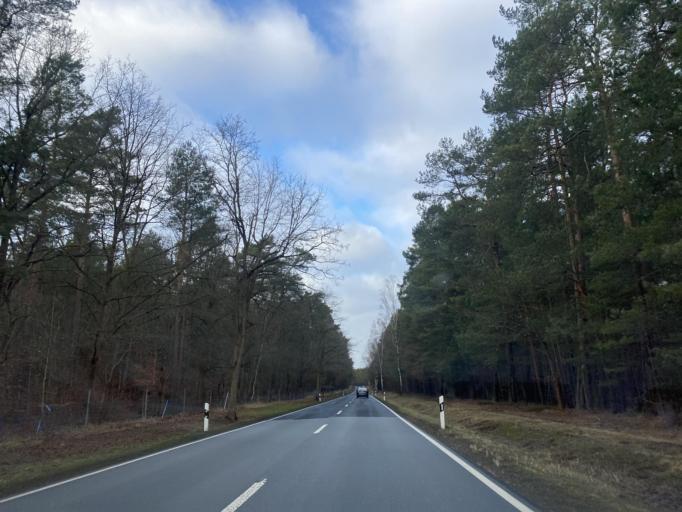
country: PL
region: Lubusz
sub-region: Powiat zarski
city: Leknica
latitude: 51.4948
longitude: 14.8266
